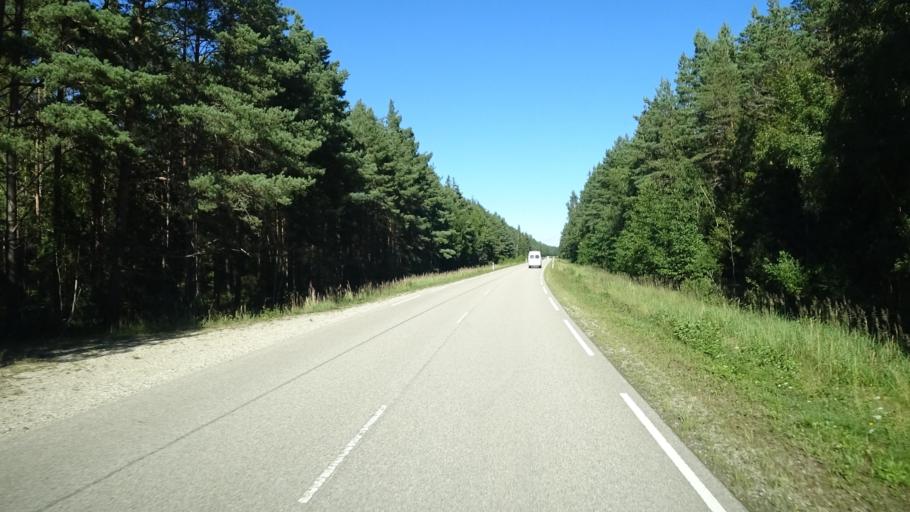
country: LV
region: Dundaga
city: Dundaga
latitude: 57.7388
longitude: 22.5337
